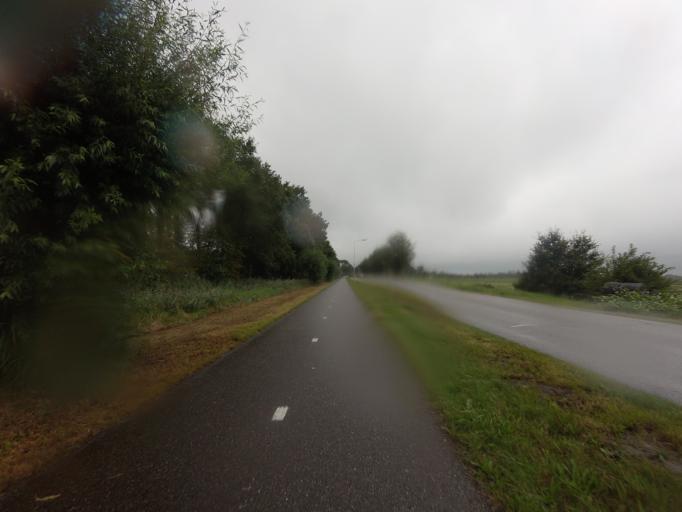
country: NL
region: Friesland
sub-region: Gemeente Tytsjerksteradiel
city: Garyp
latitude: 53.1344
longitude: 5.9453
